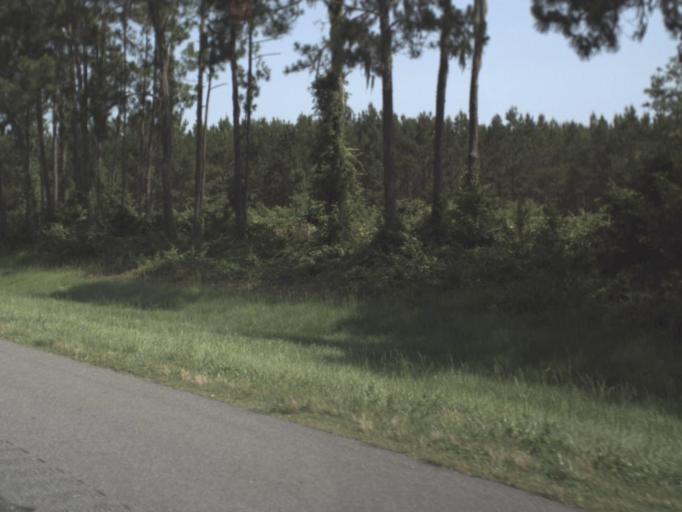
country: US
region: Florida
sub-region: Hamilton County
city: Jasper
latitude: 30.4436
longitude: -82.9244
